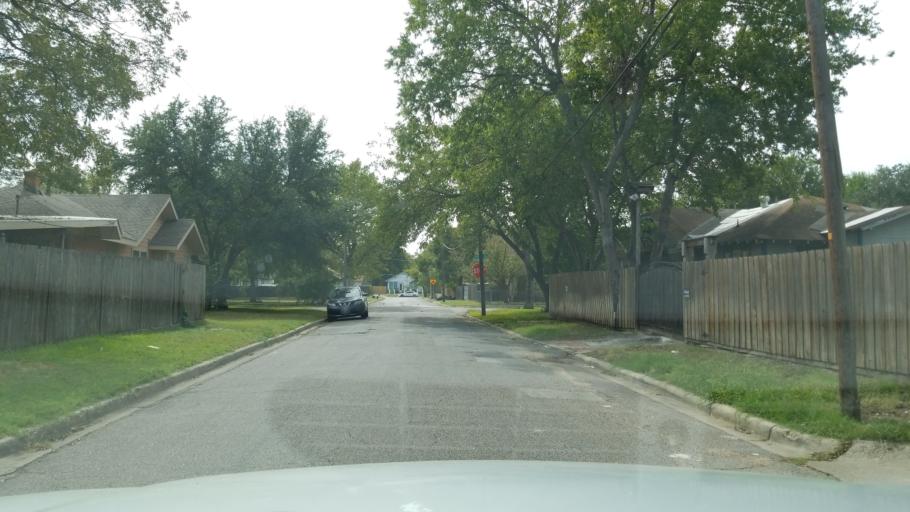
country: US
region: Texas
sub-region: Dallas County
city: Dallas
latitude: 32.7870
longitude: -96.7432
